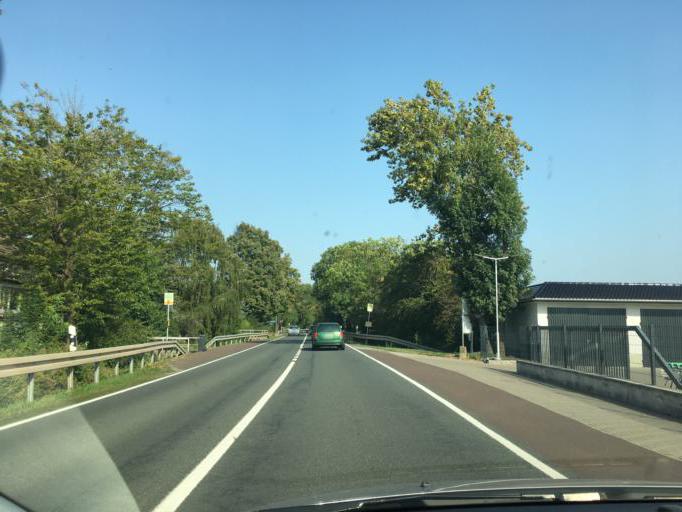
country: DE
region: Saxony-Anhalt
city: Calbe
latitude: 51.9415
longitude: 11.7625
